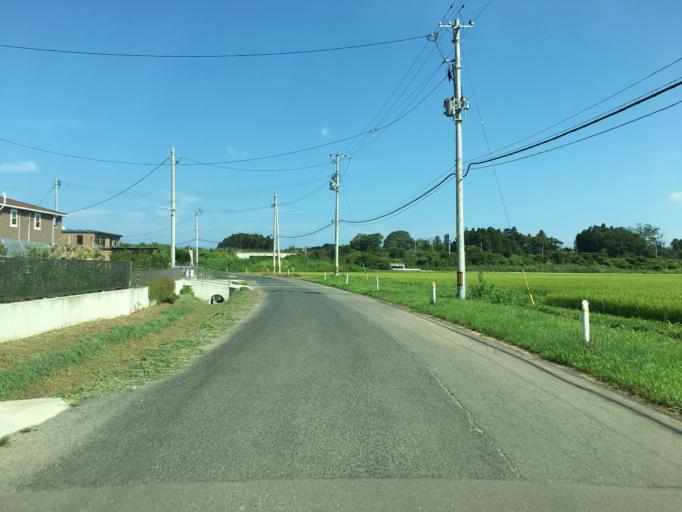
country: JP
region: Miyagi
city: Marumori
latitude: 37.7887
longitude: 140.9419
